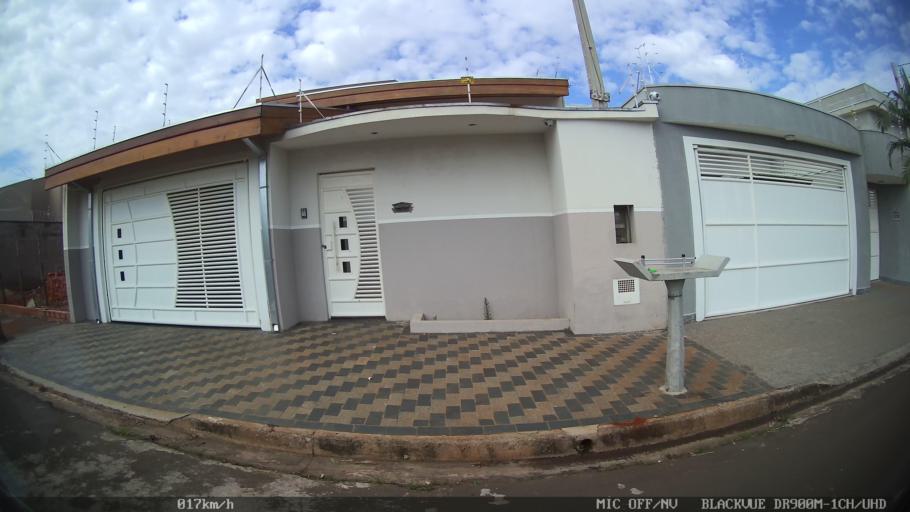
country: BR
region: Sao Paulo
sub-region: Americana
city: Americana
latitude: -22.7335
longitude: -47.3681
